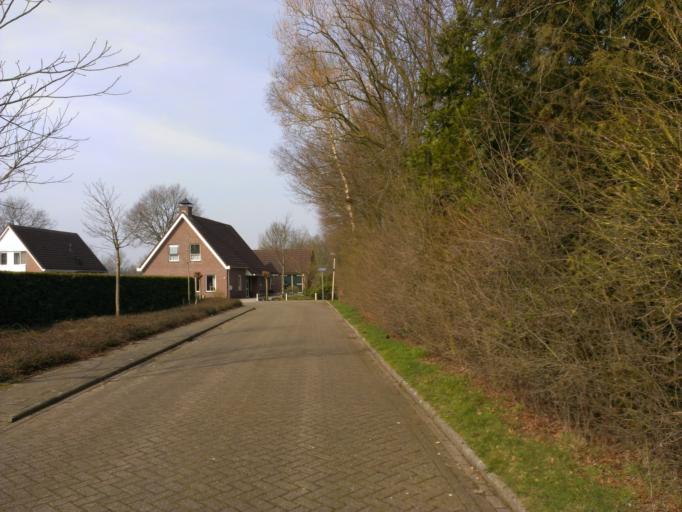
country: NL
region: Drenthe
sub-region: Gemeente Hoogeveen
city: Hoogeveen
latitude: 52.7486
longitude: 6.4994
